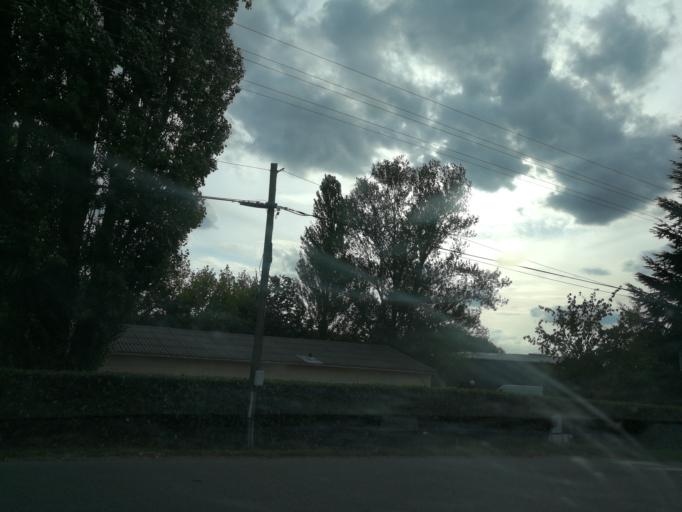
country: FR
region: Midi-Pyrenees
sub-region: Departement de la Haute-Garonne
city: Flourens
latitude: 43.6004
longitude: 1.5439
